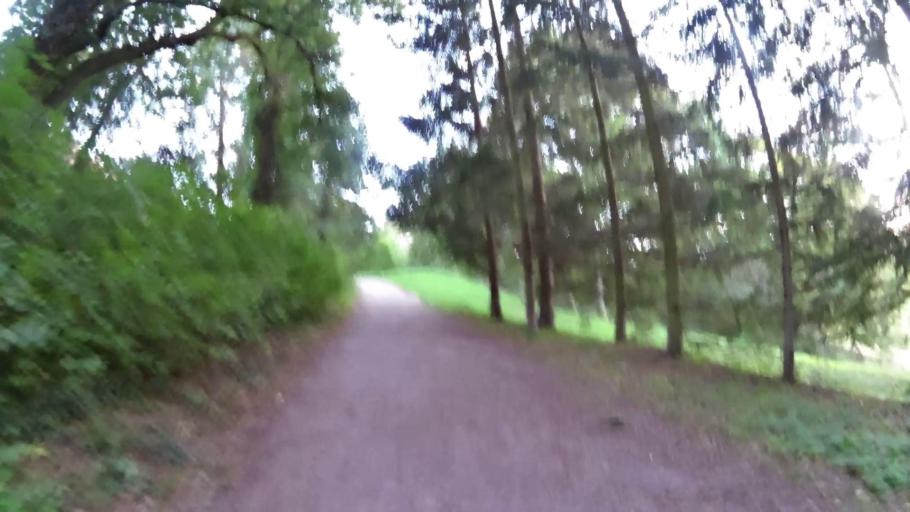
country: DE
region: Thuringia
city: Weimar
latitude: 50.9743
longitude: 11.3386
